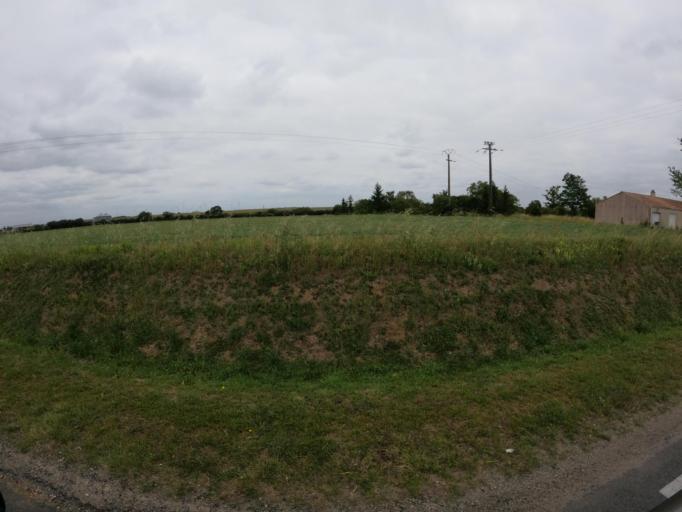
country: FR
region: Pays de la Loire
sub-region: Departement de la Vendee
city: Saint-Hilaire-des-Loges
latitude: 46.4042
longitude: -0.6744
